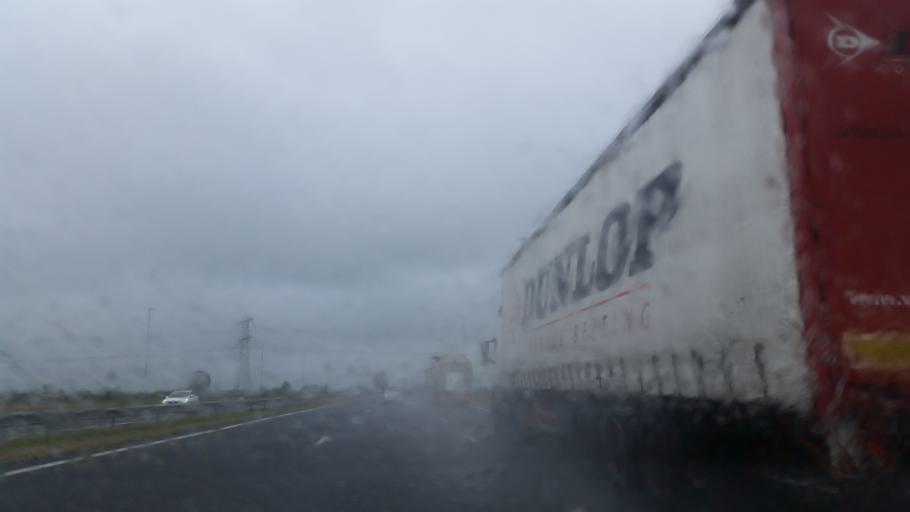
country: NL
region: Friesland
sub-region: Gemeente Leeuwarden
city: Wirdum
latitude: 53.1545
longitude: 5.7915
